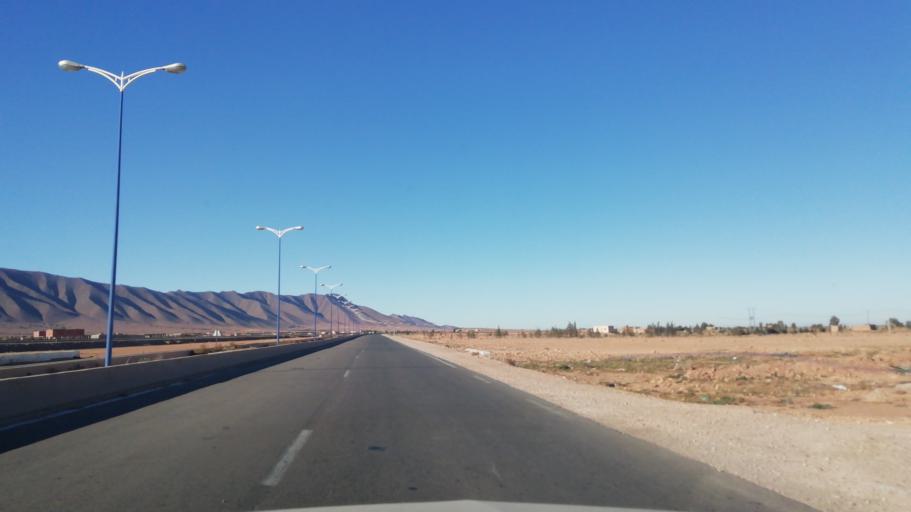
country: DZ
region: Wilaya de Naama
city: Naama
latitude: 33.5635
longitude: -0.2385
